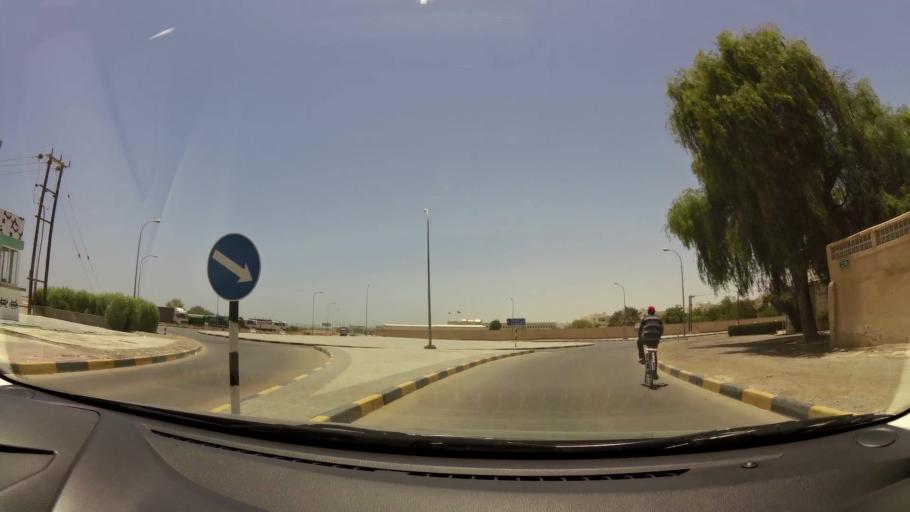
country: OM
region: Muhafazat Masqat
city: As Sib al Jadidah
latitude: 23.6307
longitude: 58.2477
